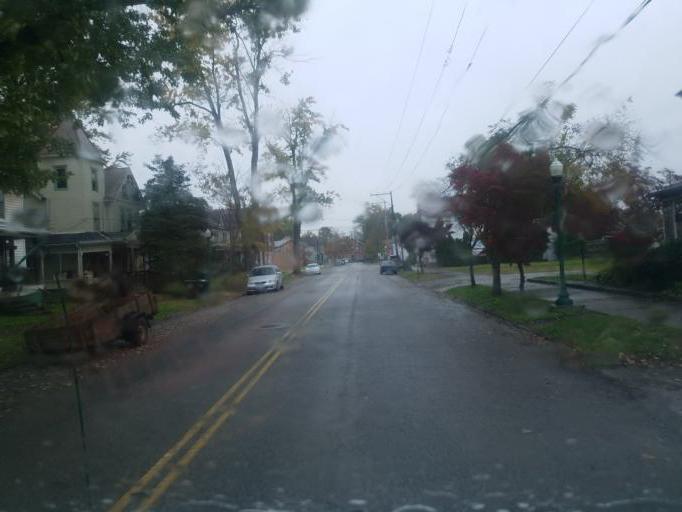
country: US
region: Ohio
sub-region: Washington County
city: Marietta
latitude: 39.4124
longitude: -81.4610
